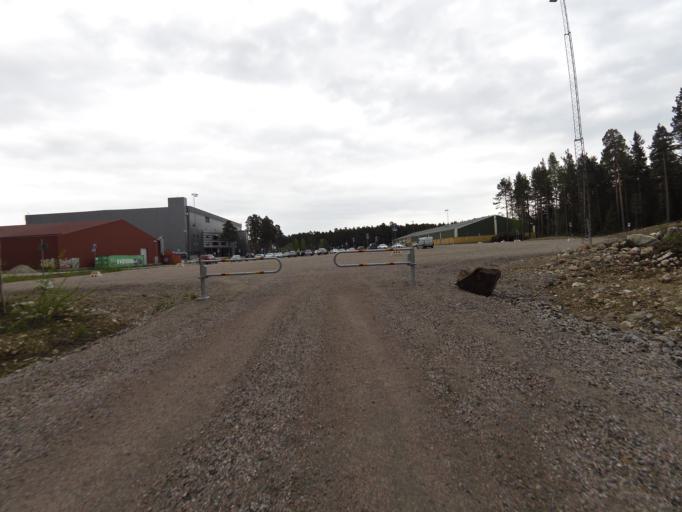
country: SE
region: Gaevleborg
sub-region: Gavle Kommun
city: Gavle
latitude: 60.6920
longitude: 17.1287
